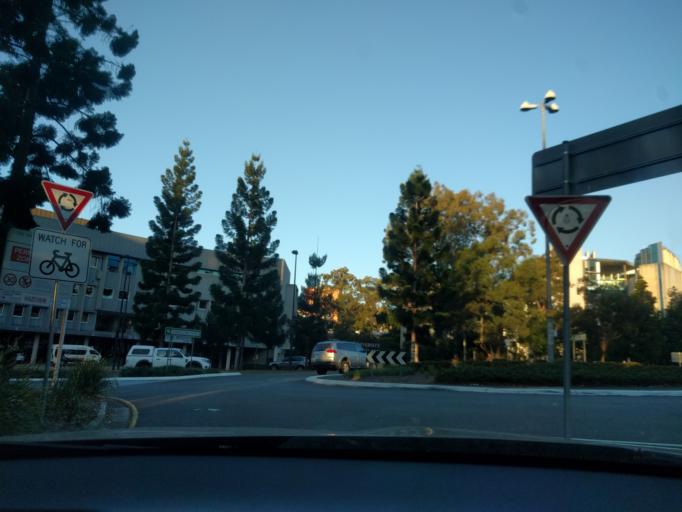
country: AU
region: Queensland
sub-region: Brisbane
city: Yeronga
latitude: -27.4988
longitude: 153.0106
